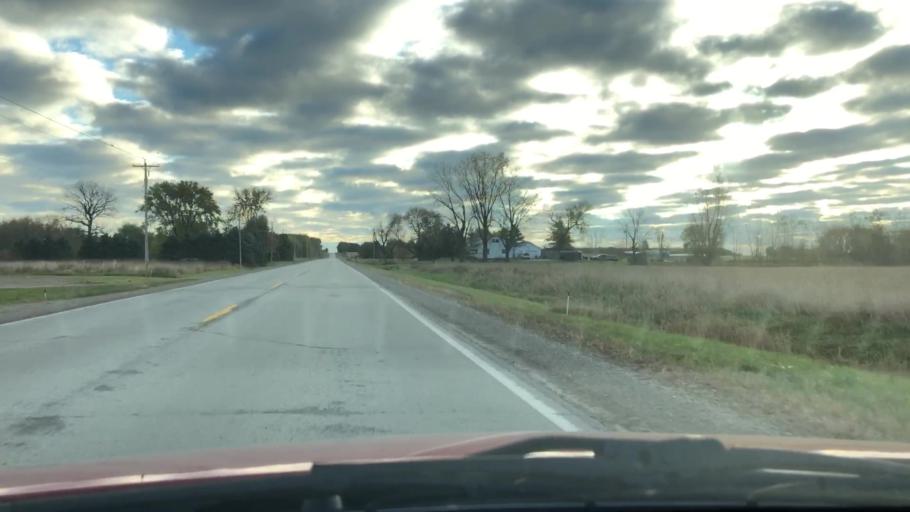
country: US
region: Wisconsin
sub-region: Outagamie County
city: Seymour
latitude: 44.4440
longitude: -88.2818
